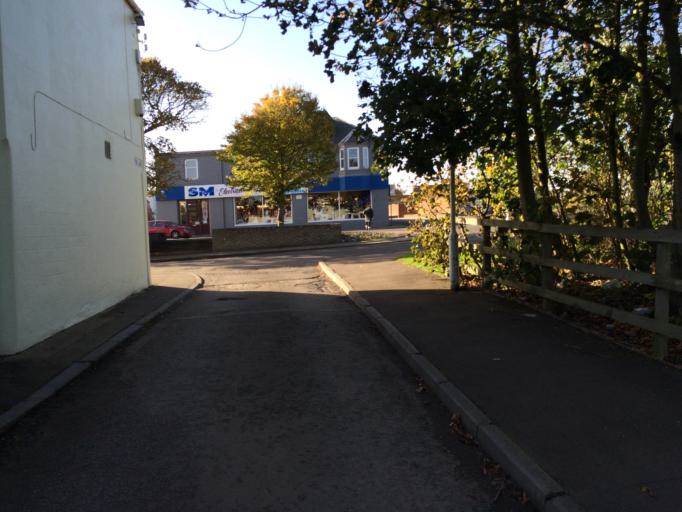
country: GB
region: Scotland
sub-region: Fife
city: Kirkcaldy
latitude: 56.1346
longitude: -3.1313
